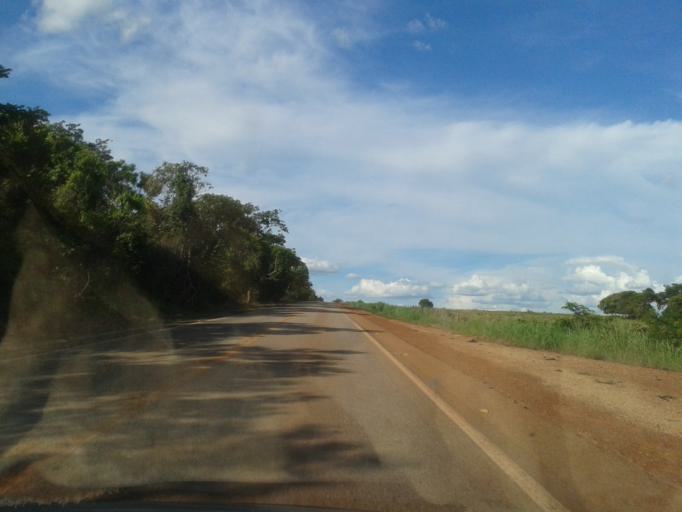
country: BR
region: Goias
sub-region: Mozarlandia
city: Mozarlandia
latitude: -14.3984
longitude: -50.4418
